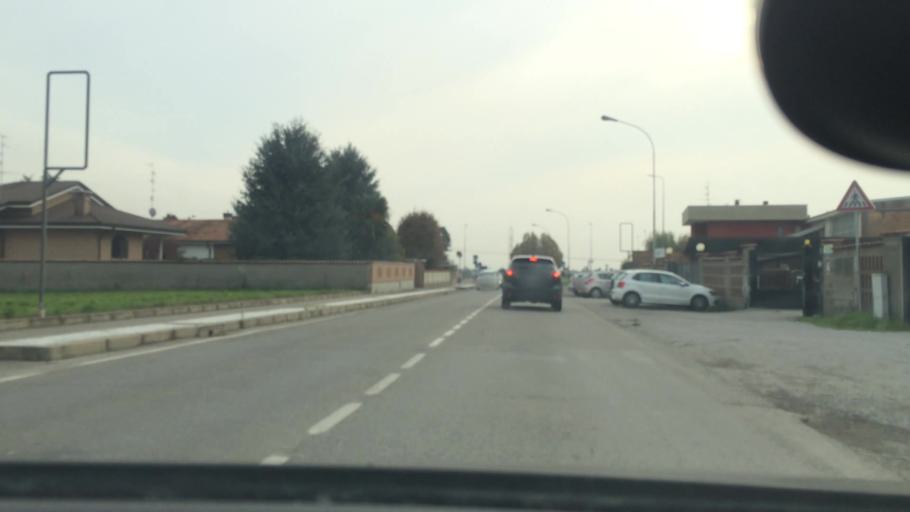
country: IT
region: Lombardy
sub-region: Provincia di Monza e Brianza
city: Misinto
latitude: 45.6595
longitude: 9.0736
